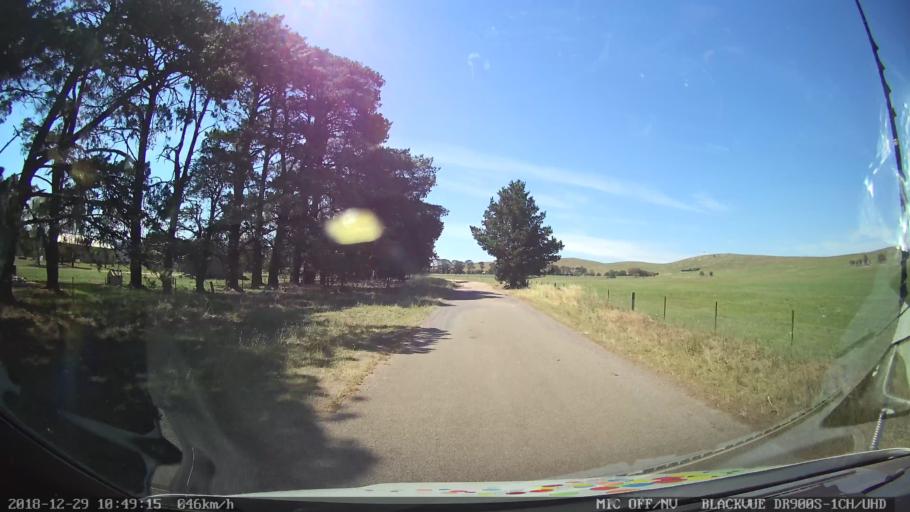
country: AU
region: New South Wales
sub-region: Palerang
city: Bungendore
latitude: -35.0743
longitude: 149.5148
